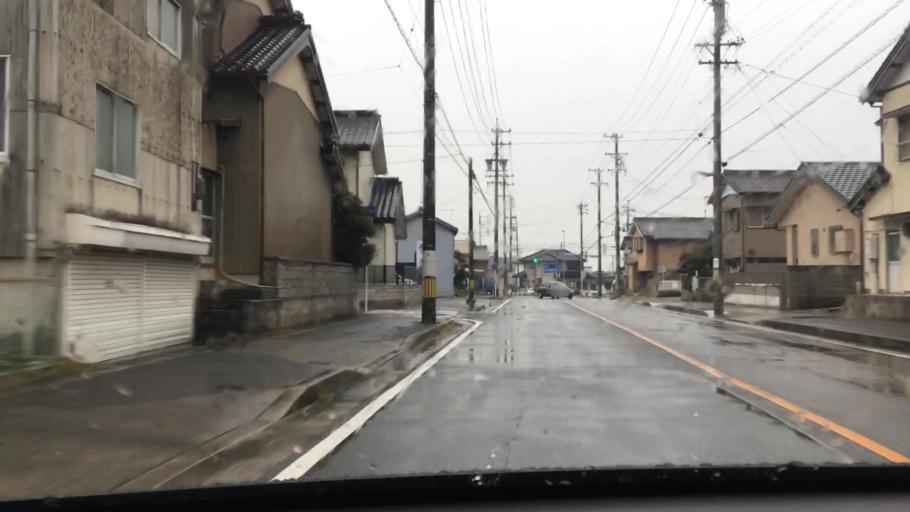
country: JP
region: Aichi
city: Gamagori
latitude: 34.8168
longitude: 137.2548
